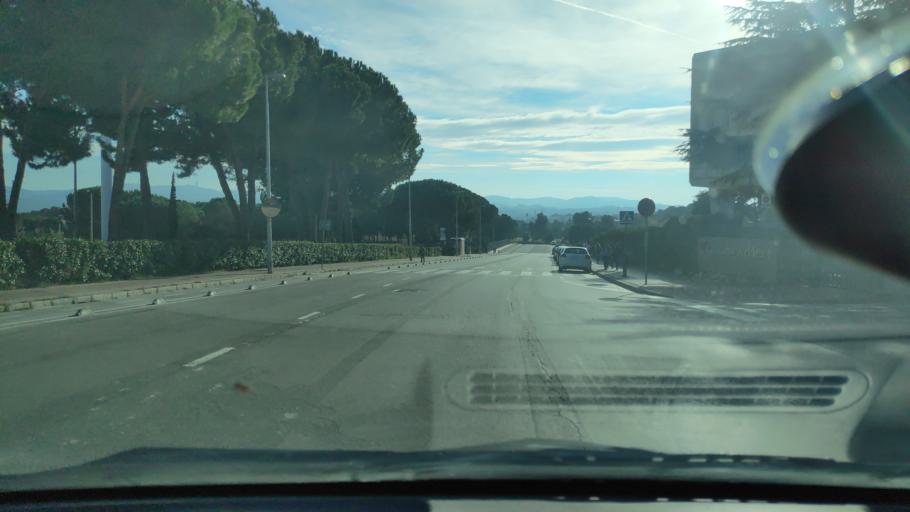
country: ES
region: Catalonia
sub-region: Provincia de Barcelona
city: Sant Cugat del Valles
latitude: 41.4896
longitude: 2.0777
